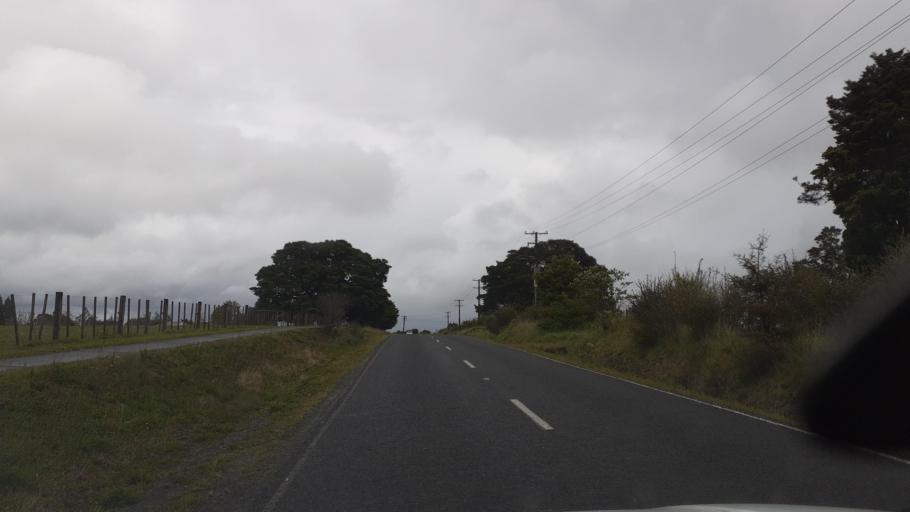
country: NZ
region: Northland
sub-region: Far North District
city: Waimate North
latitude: -35.4176
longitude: 173.7977
